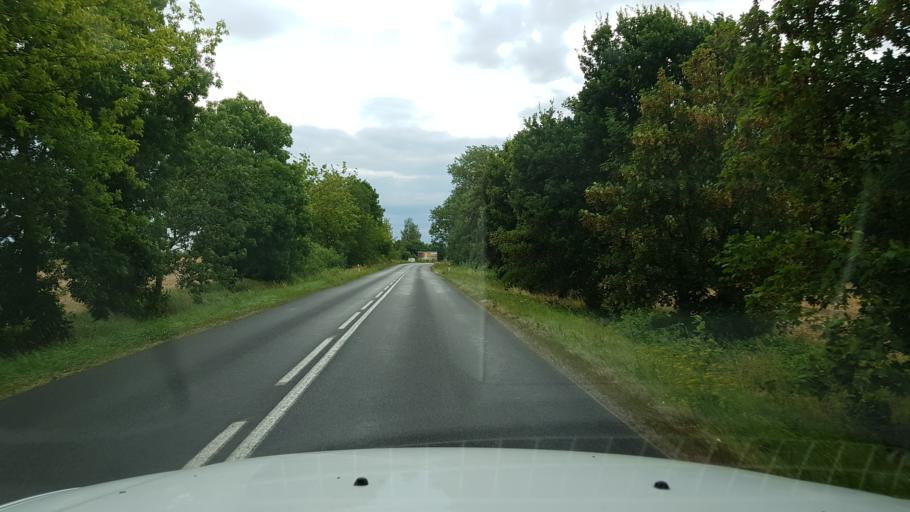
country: PL
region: West Pomeranian Voivodeship
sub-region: Powiat kolobrzeski
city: Dygowo
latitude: 54.1460
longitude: 15.6497
